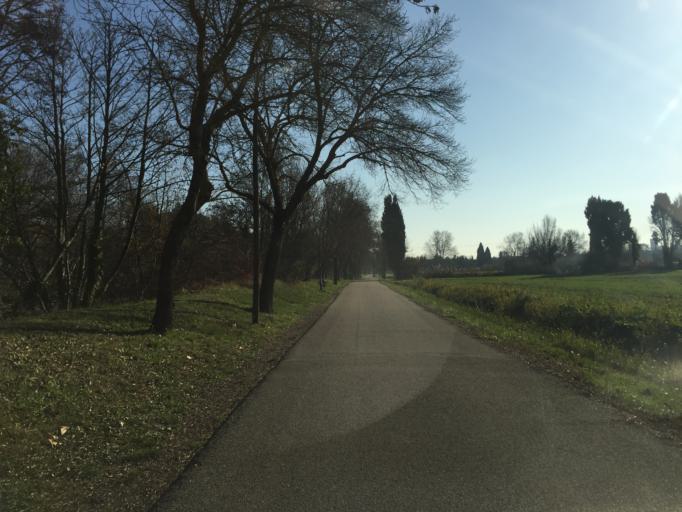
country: FR
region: Provence-Alpes-Cote d'Azur
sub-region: Departement du Vaucluse
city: Entraigues-sur-la-Sorgue
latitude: 44.0118
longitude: 4.9251
